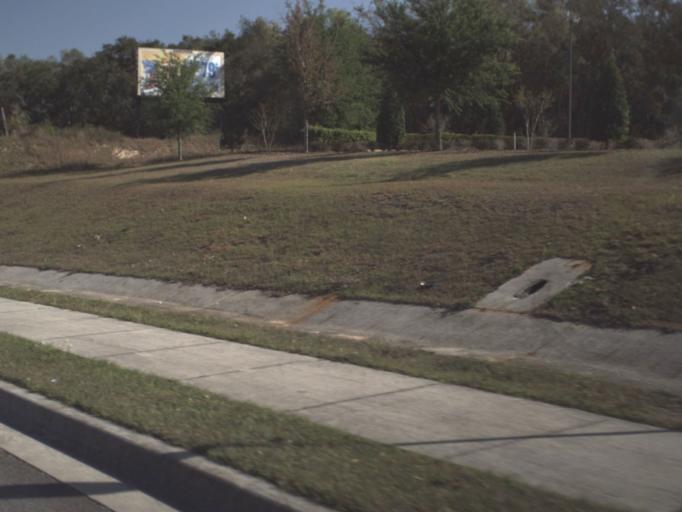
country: US
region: Florida
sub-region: Lake County
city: Minneola
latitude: 28.5554
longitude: -81.7427
